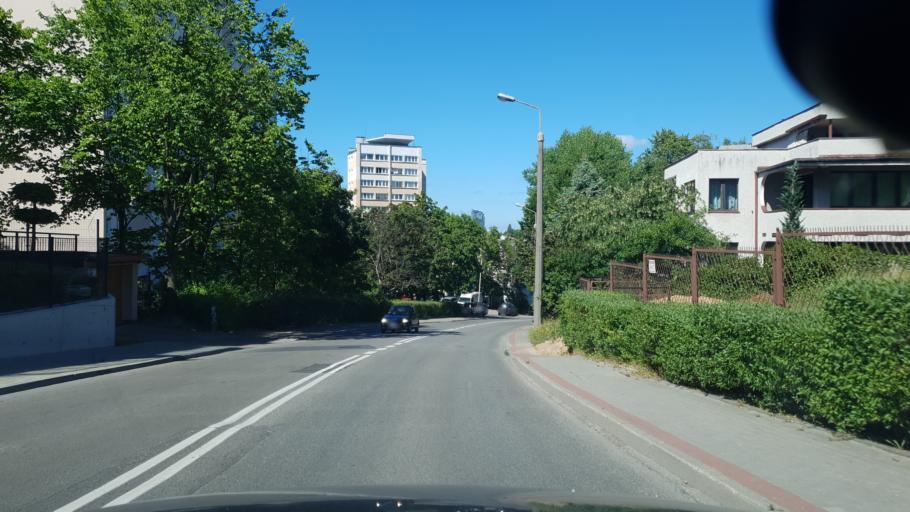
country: PL
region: Pomeranian Voivodeship
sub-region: Gdynia
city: Gdynia
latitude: 54.5052
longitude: 18.5430
